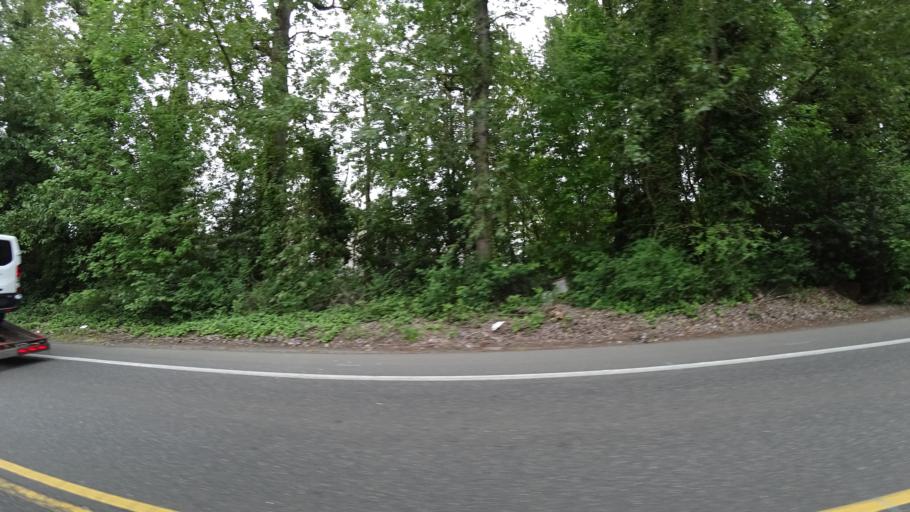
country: US
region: Washington
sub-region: Clark County
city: Vancouver
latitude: 45.6023
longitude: -122.6721
